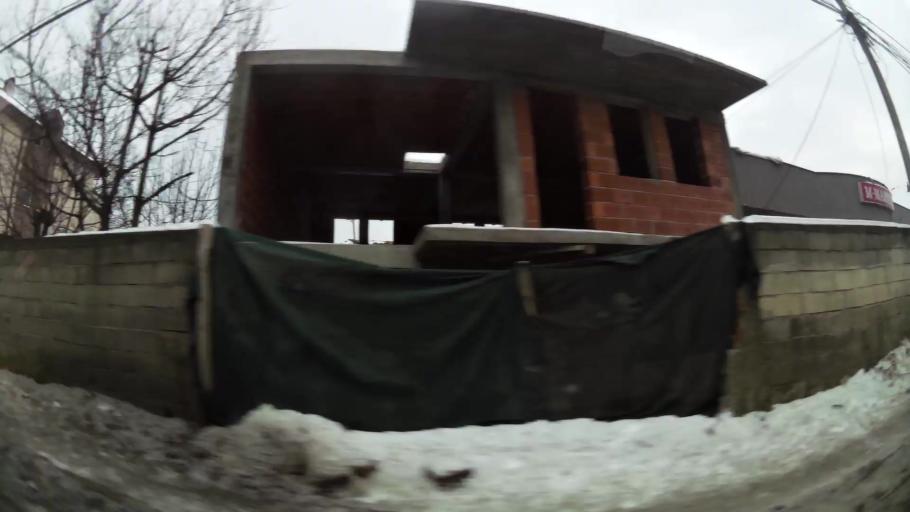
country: MK
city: Kondovo
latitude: 42.0111
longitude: 21.3158
